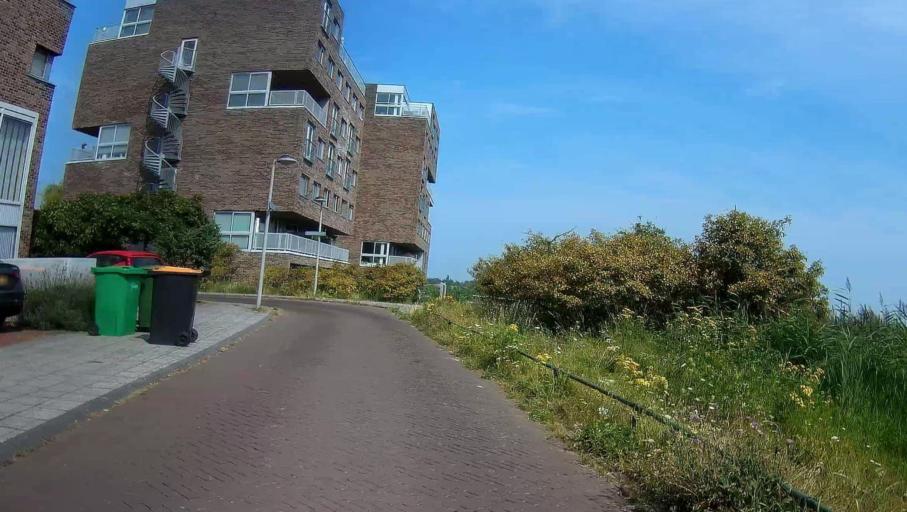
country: NL
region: South Holland
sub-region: Gemeente Pijnacker-Nootdorp
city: Pijnacker
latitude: 52.0626
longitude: 4.4201
